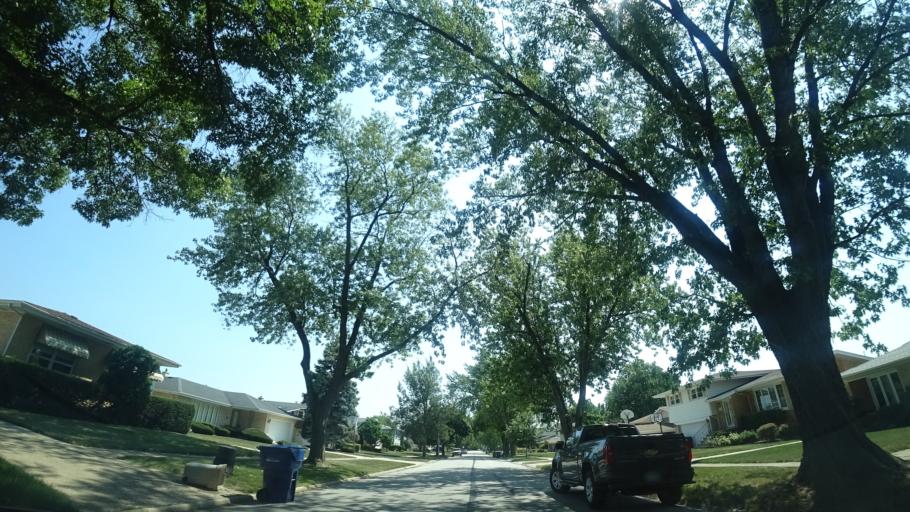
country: US
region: Illinois
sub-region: Cook County
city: Oak Lawn
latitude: 41.7034
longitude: -87.7548
